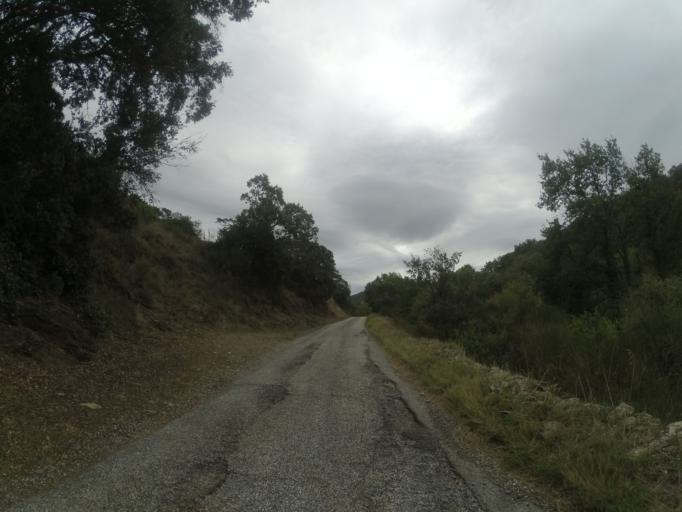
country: FR
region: Languedoc-Roussillon
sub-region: Departement des Pyrenees-Orientales
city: Estagel
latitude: 42.7446
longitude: 2.6774
